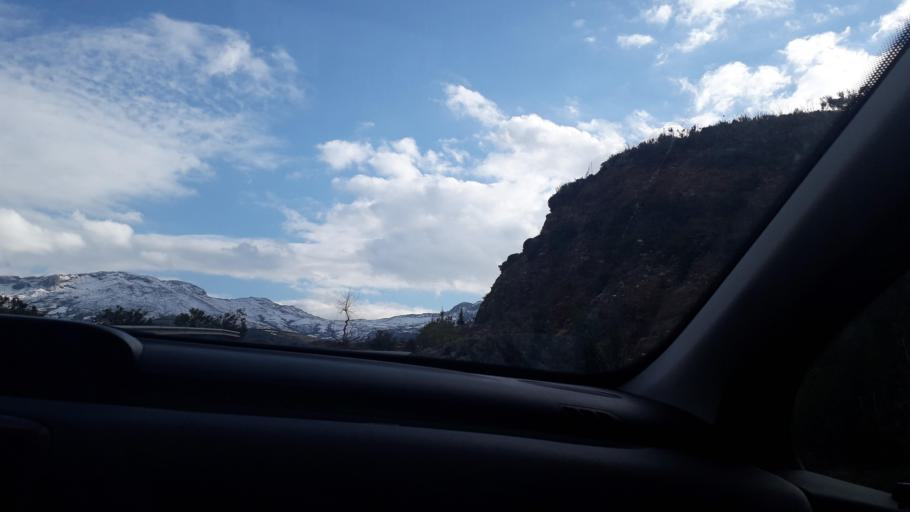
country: GR
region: Crete
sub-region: Nomos Rethymnis
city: Agia Foteini
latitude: 35.2776
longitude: 24.5622
